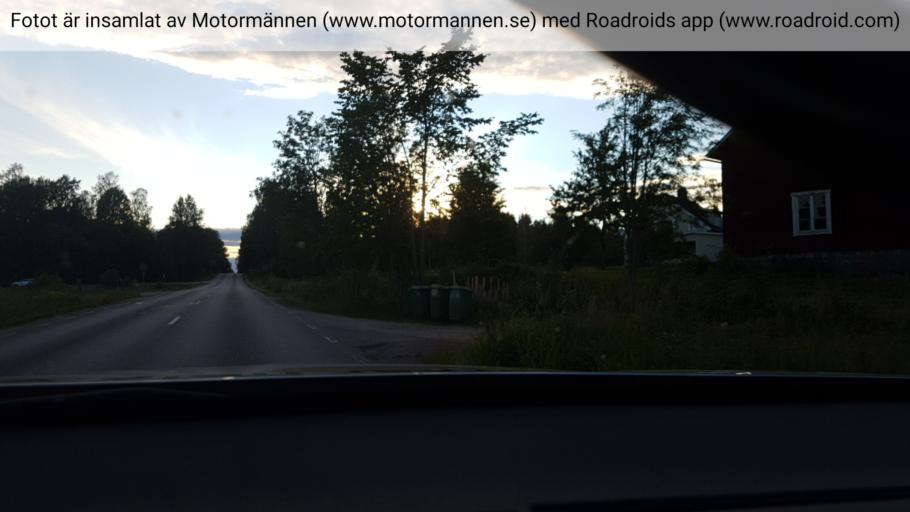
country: SE
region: Vaermland
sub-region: Torsby Kommun
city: Torsby
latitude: 60.1319
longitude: 13.0523
